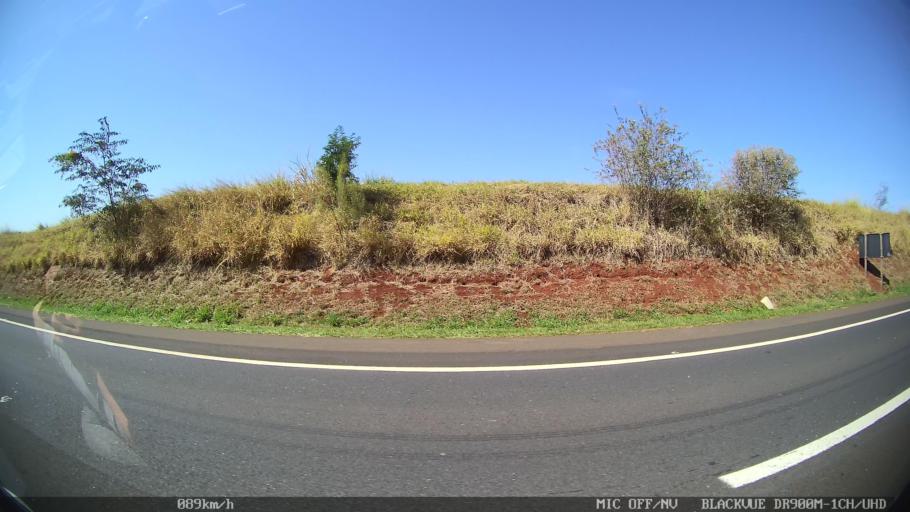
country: BR
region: Sao Paulo
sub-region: Batatais
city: Batatais
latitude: -20.7926
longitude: -47.5617
